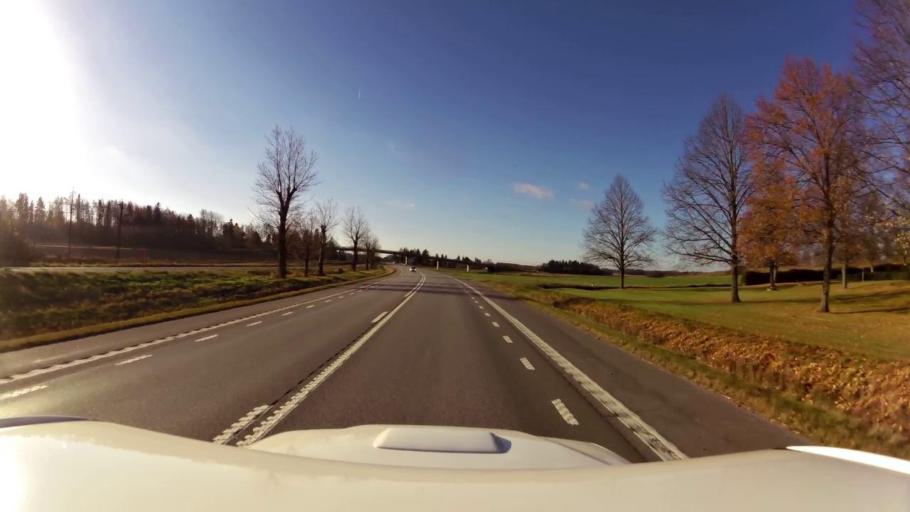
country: SE
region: OEstergoetland
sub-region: Linkopings Kommun
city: Linghem
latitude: 58.4505
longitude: 15.8295
